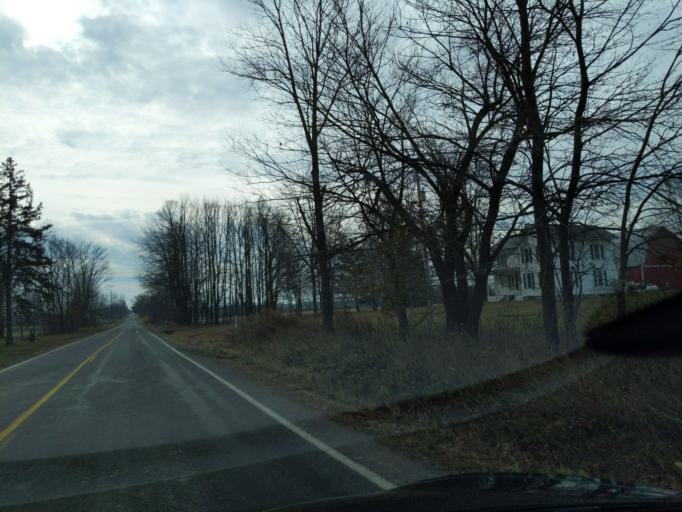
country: US
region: Michigan
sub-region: Ingham County
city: Leslie
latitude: 42.5050
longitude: -84.5219
